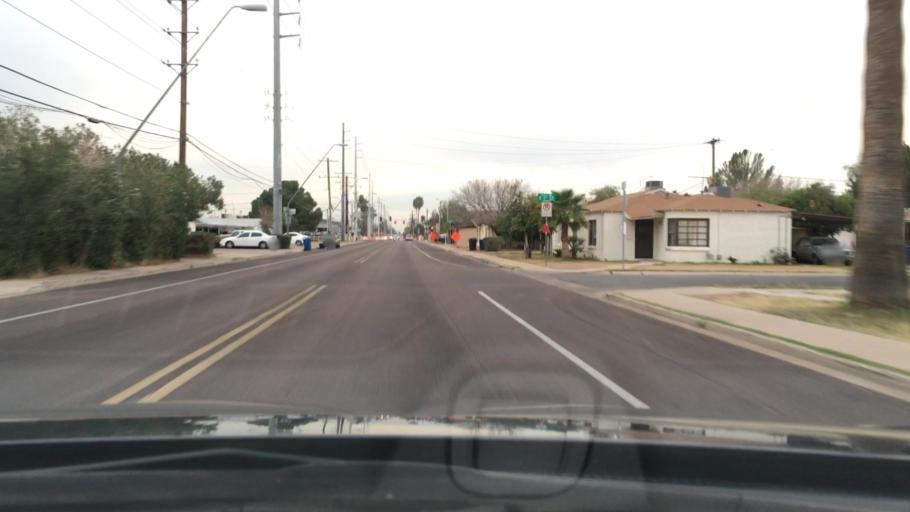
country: US
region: Arizona
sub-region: Maricopa County
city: Mesa
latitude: 33.4176
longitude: -111.8141
